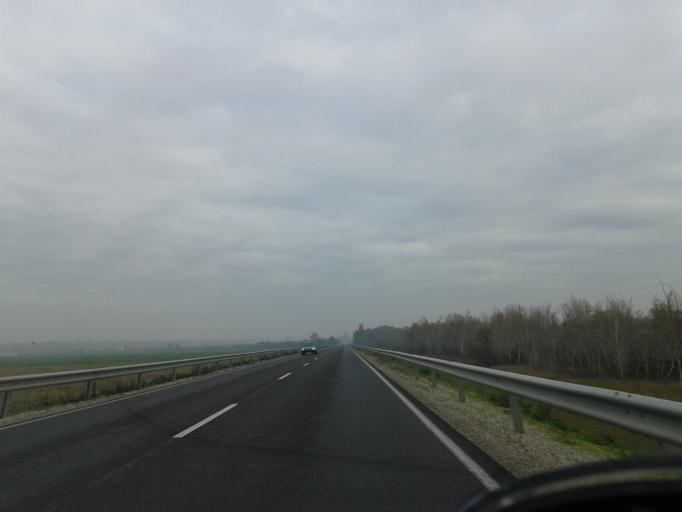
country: HU
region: Fejer
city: Ercsi
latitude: 47.2229
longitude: 18.8895
